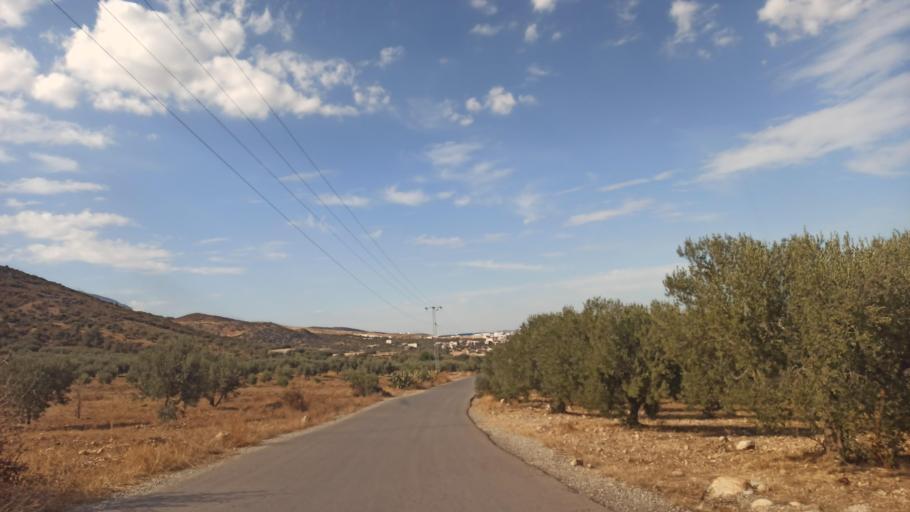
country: TN
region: Zaghwan
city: Zaghouan
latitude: 36.3362
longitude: 10.2111
